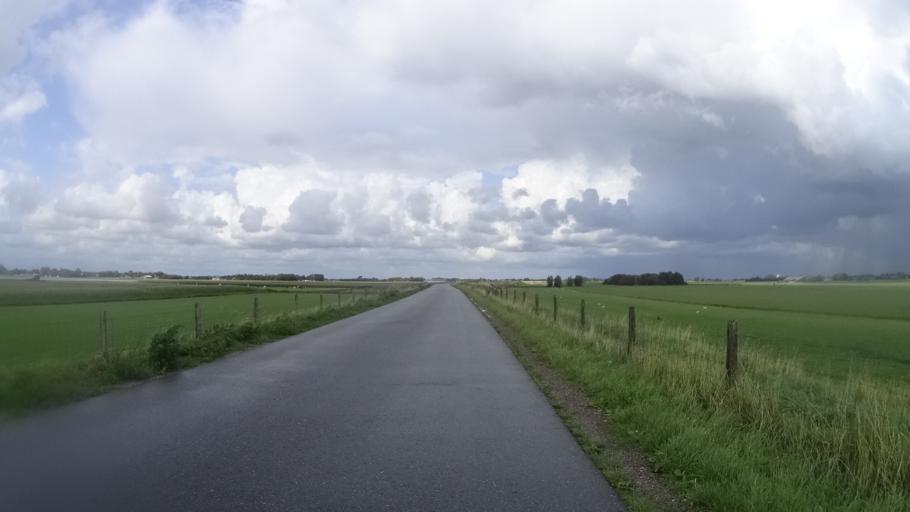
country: NL
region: North Holland
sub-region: Gemeente Schagen
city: Harenkarspel
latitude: 52.7776
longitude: 4.7426
